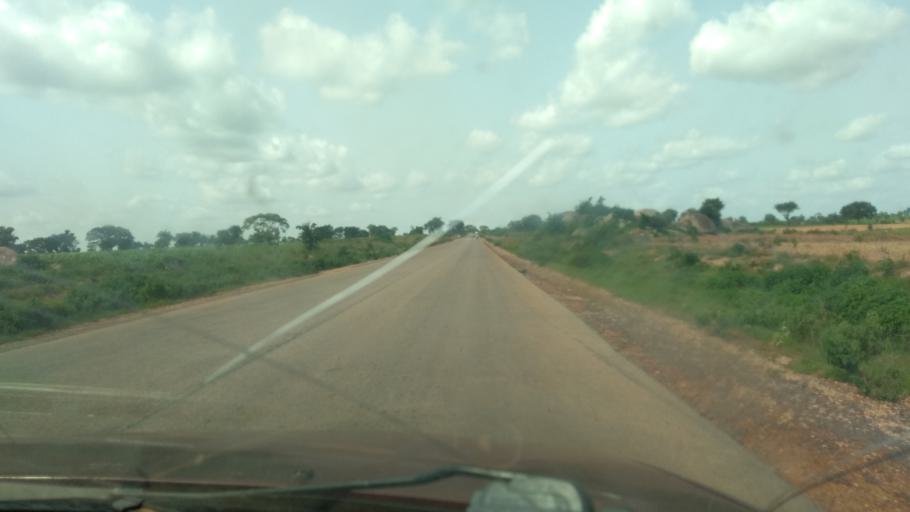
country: NG
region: Katsina
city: Sabuwa
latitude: 11.0503
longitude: 7.1590
